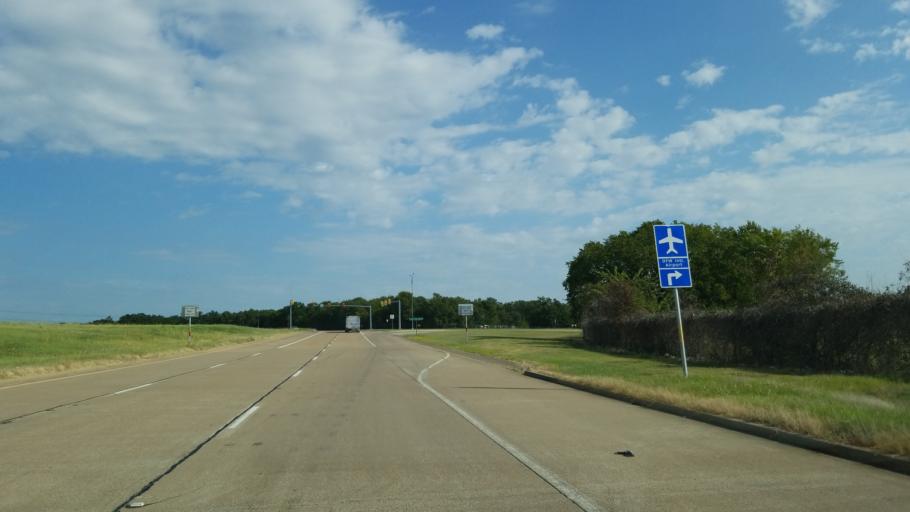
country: US
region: Texas
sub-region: Tarrant County
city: Euless
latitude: 32.8657
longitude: -97.0634
